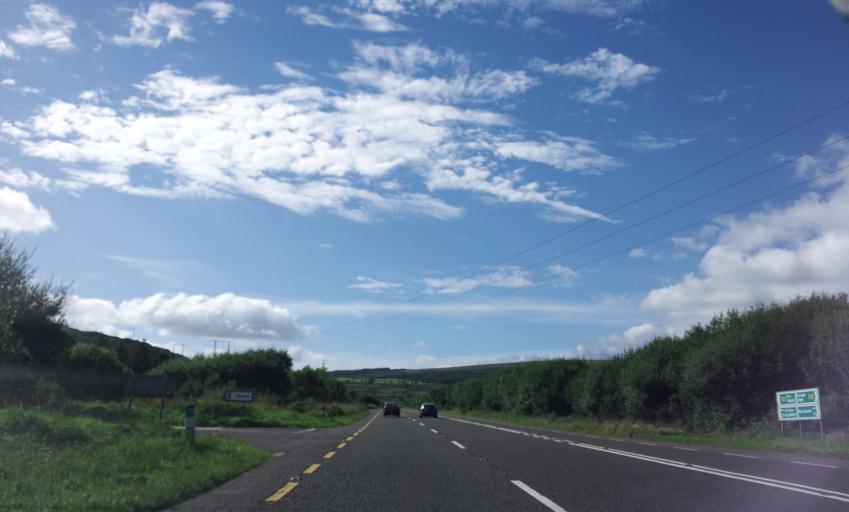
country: IE
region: Munster
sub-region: County Cork
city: Millstreet
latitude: 51.9582
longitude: -9.1935
